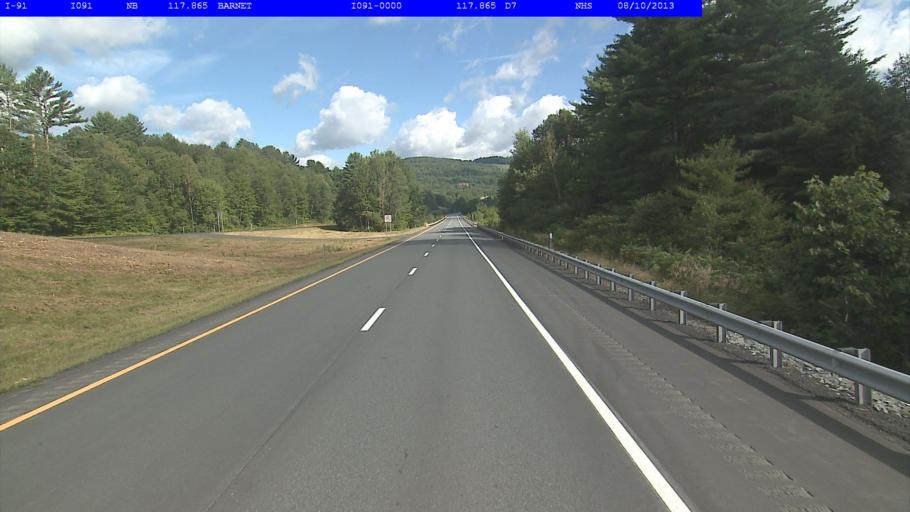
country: US
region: New Hampshire
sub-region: Grafton County
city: Woodsville
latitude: 44.2640
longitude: -72.0682
